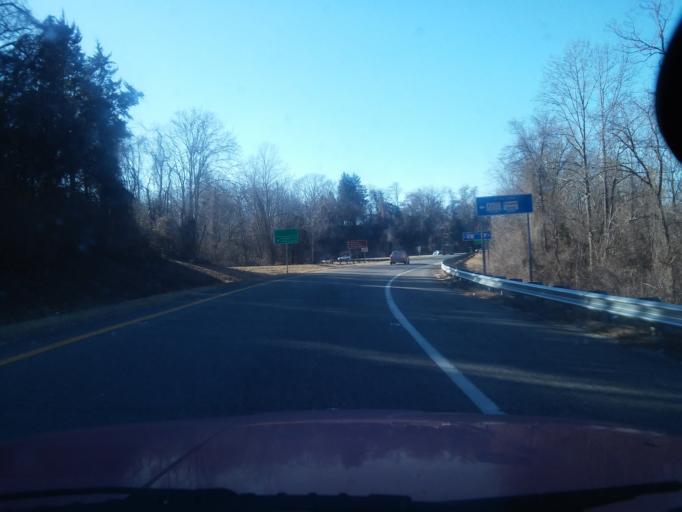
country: US
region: Virginia
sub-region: City of Charlottesville
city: Charlottesville
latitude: 38.0124
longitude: -78.4737
